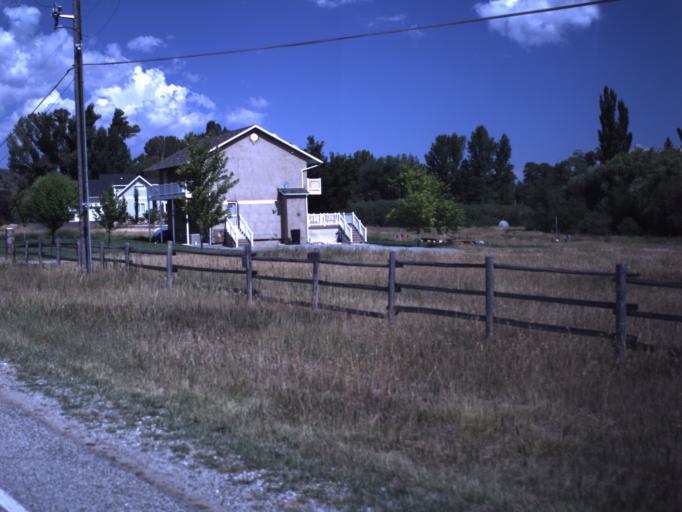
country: US
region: Idaho
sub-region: Bear Lake County
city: Paris
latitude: 41.9833
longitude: -111.4096
